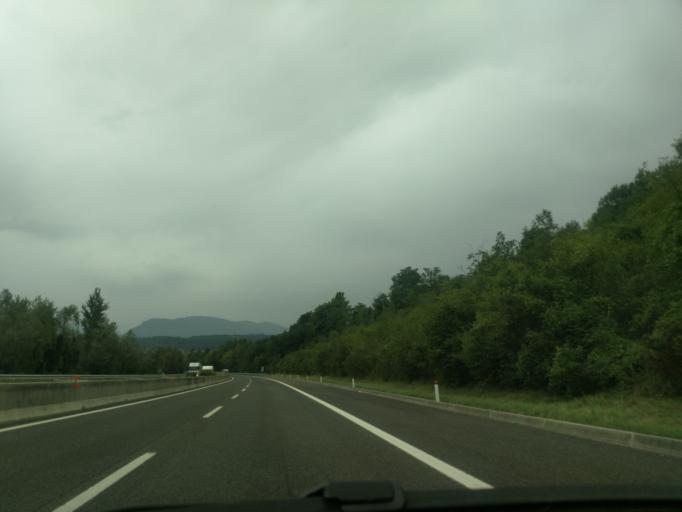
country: IT
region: Veneto
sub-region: Provincia di Belluno
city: Ponte nelle Alpi-Polpet
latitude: 46.1920
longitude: 12.2895
